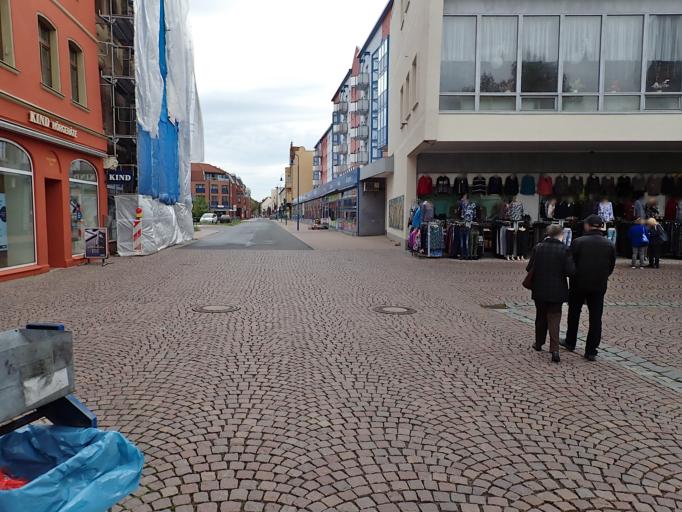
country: DE
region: Saxony
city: Bitterfeld-Wolfen
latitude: 51.6239
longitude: 12.3306
